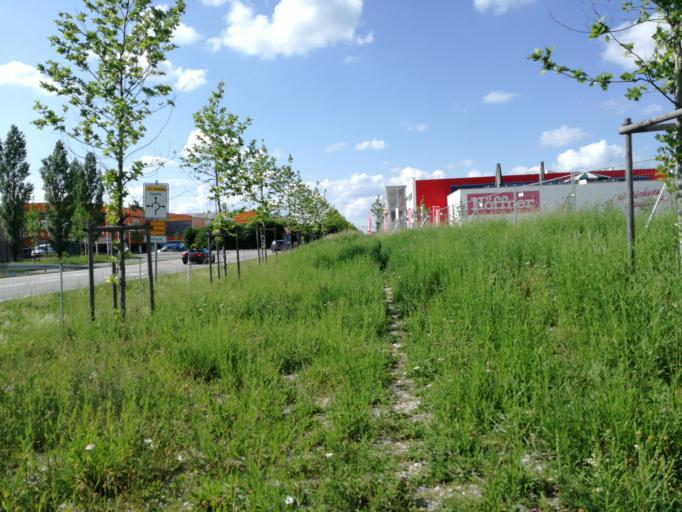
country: DE
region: Bavaria
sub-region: Upper Bavaria
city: Grafelfing
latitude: 48.1311
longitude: 11.4135
